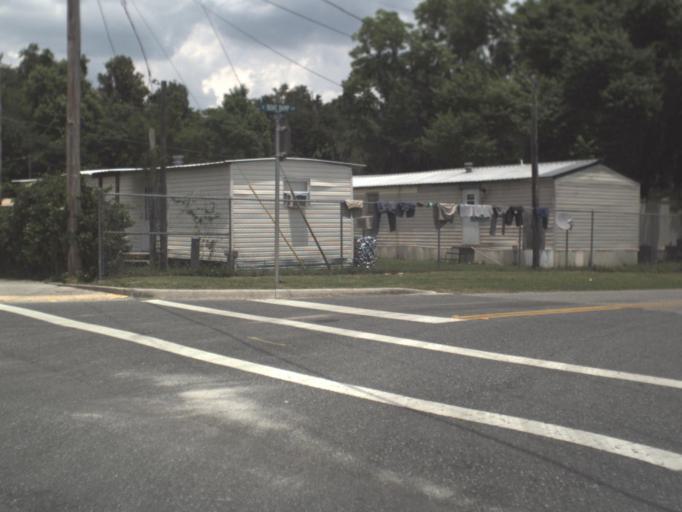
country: US
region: Florida
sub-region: Columbia County
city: Lake City
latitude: 30.1534
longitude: -82.6397
